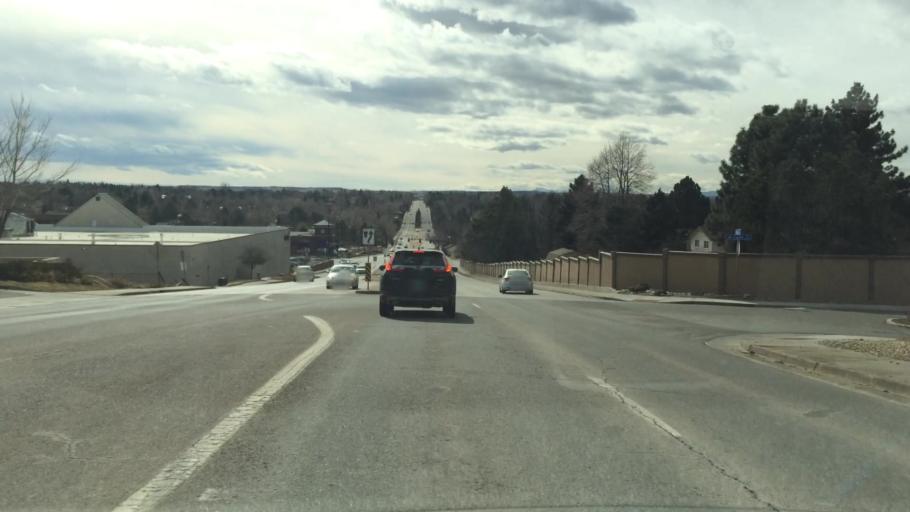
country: US
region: Colorado
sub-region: Arapahoe County
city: Castlewood
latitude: 39.5973
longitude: -104.9042
